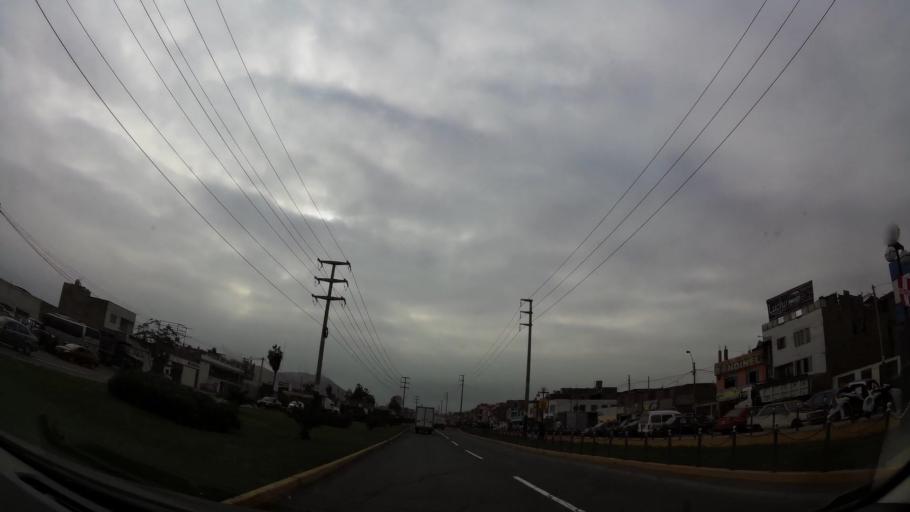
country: PE
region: Lima
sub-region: Lima
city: Surco
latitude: -12.1996
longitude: -76.9969
